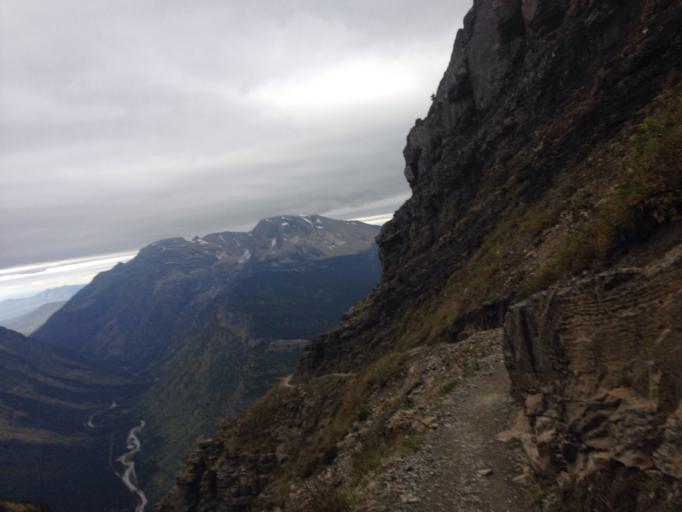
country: US
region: Montana
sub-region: Flathead County
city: Columbia Falls
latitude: 48.7436
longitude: -113.7315
